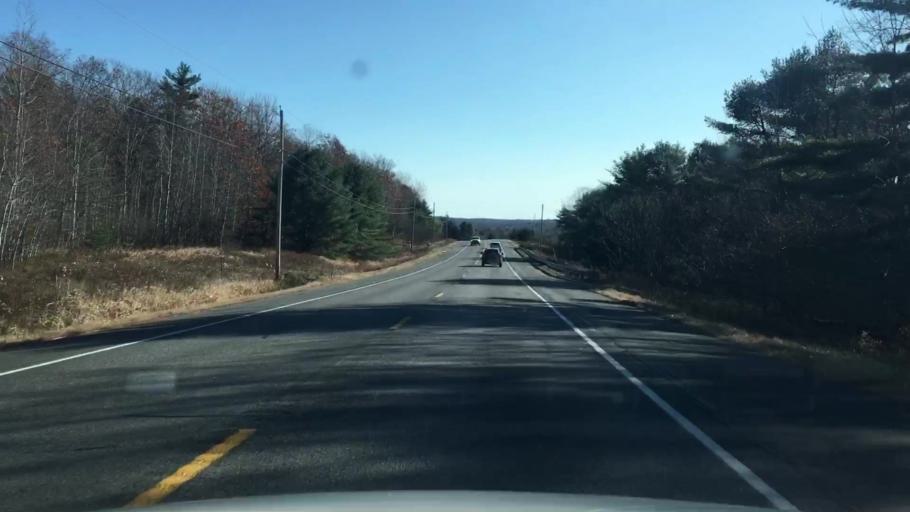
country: US
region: Maine
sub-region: Knox County
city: Union
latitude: 44.2193
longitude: -69.3173
